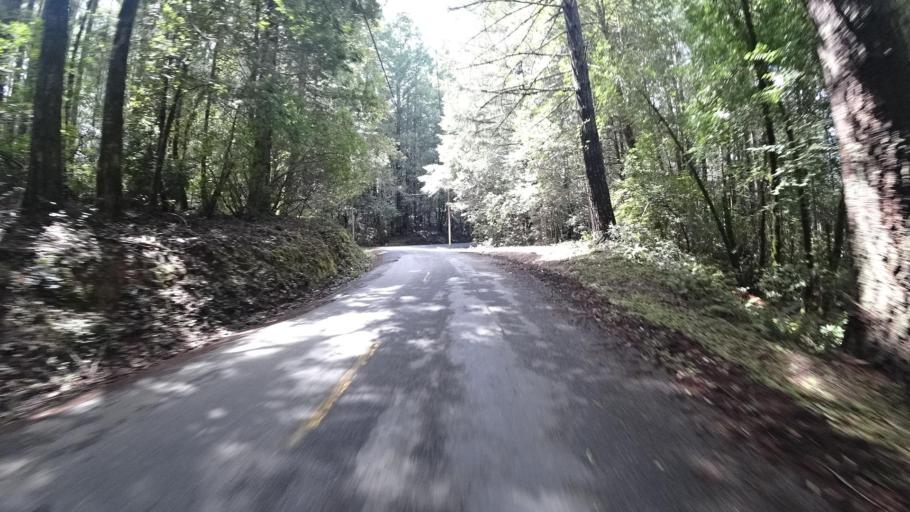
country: US
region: California
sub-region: Humboldt County
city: Blue Lake
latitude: 40.7589
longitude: -123.9681
